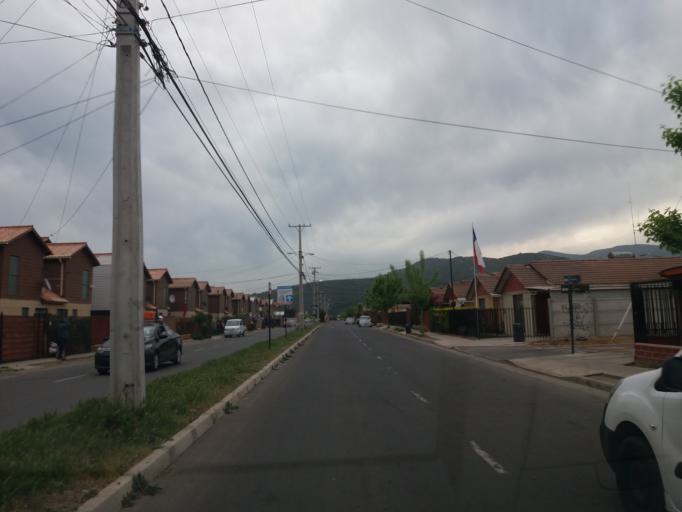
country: CL
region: Valparaiso
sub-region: Provincia de Quillota
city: Quillota
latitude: -32.8950
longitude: -71.2677
